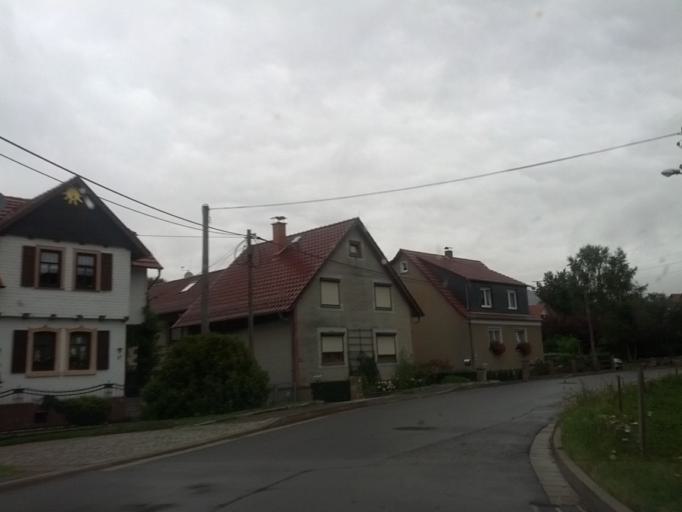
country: DE
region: Thuringia
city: Mechterstadt
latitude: 50.9358
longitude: 10.4821
